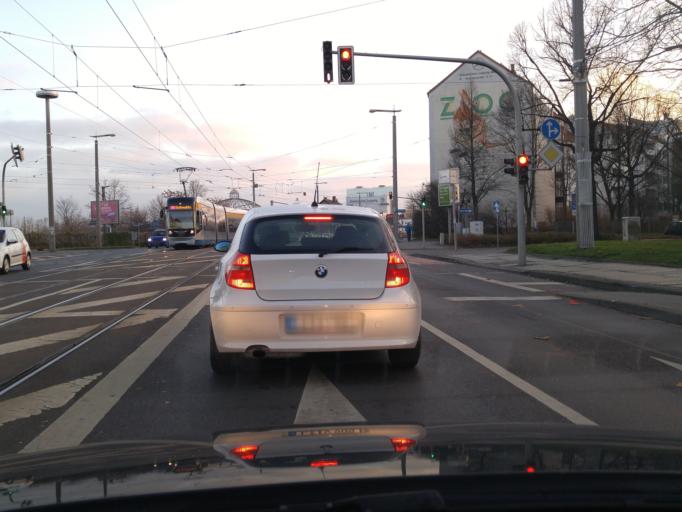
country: DE
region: Saxony
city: Leipzig
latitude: 51.3575
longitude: 12.3764
